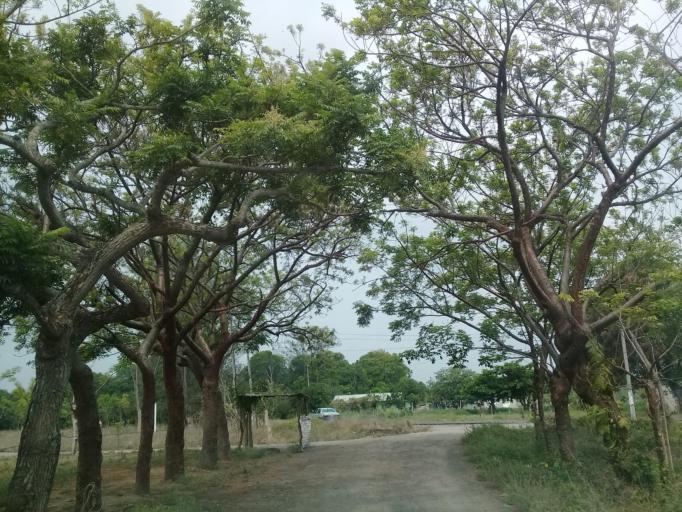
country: MX
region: Veracruz
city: Jamapa
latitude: 19.0508
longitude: -96.2059
